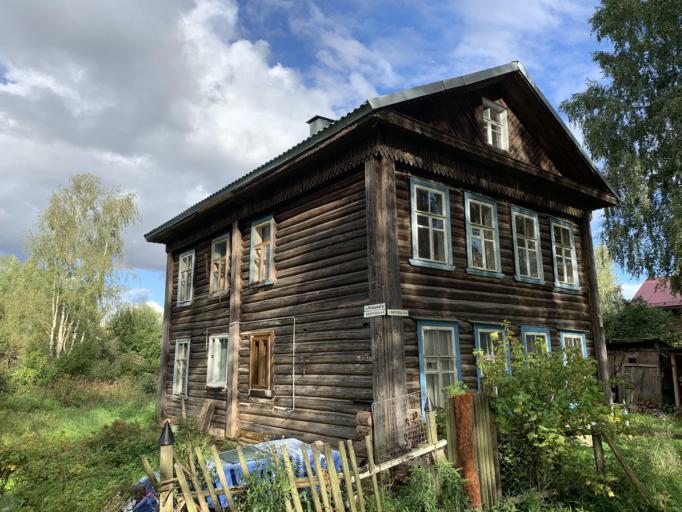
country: RU
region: Tverskaya
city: Vyshniy Volochek
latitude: 57.5874
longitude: 34.5487
